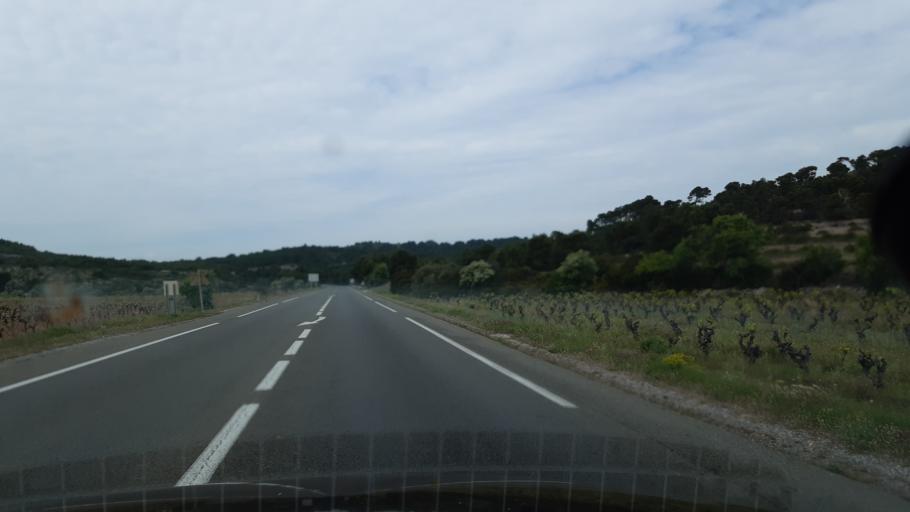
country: FR
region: Languedoc-Roussillon
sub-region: Departement de l'Aude
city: Gruissan
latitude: 43.1178
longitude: 3.0870
